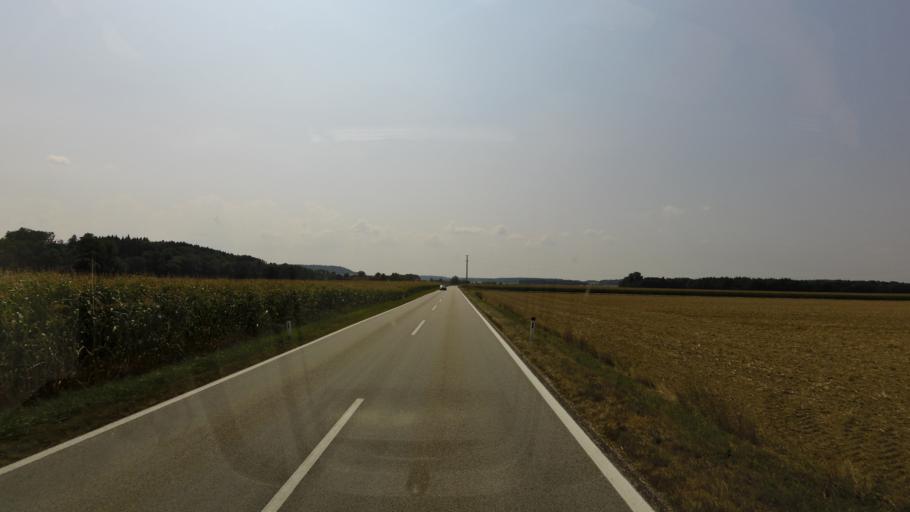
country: DE
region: Bavaria
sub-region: Lower Bavaria
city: Bad Fussing
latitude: 48.2839
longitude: 13.3287
